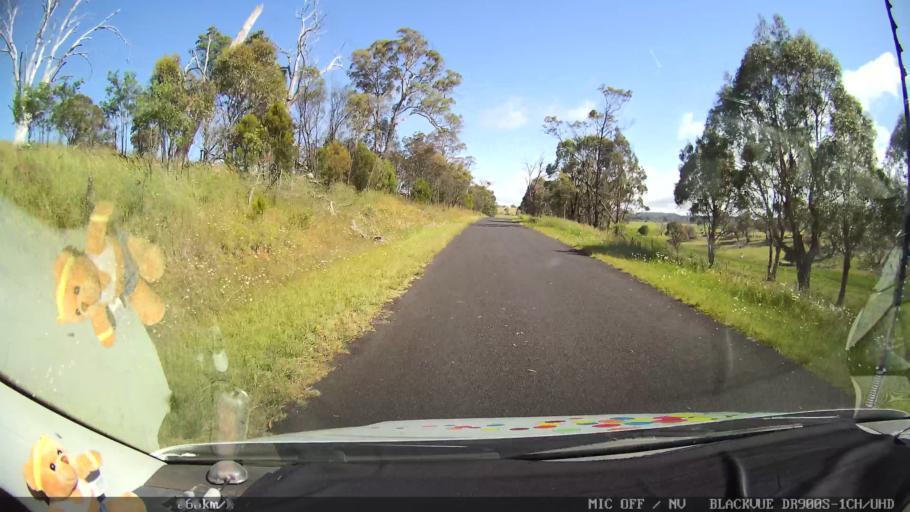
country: AU
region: New South Wales
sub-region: Guyra
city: Guyra
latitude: -30.0608
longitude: 151.6648
